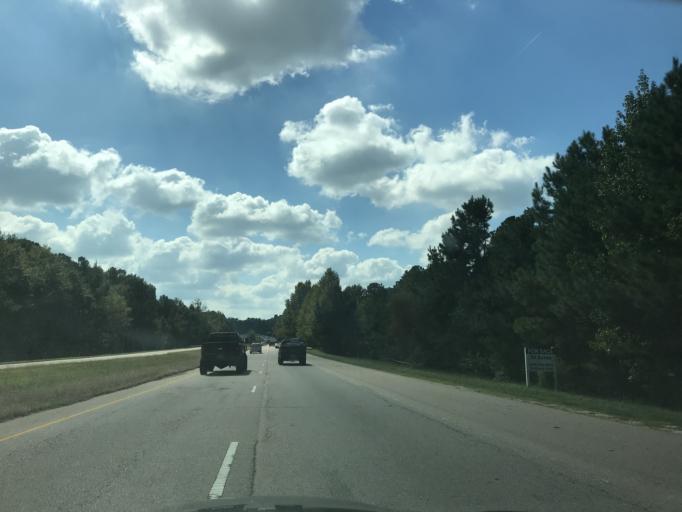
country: US
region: North Carolina
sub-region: Wake County
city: Wake Forest
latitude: 35.9118
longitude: -78.5523
